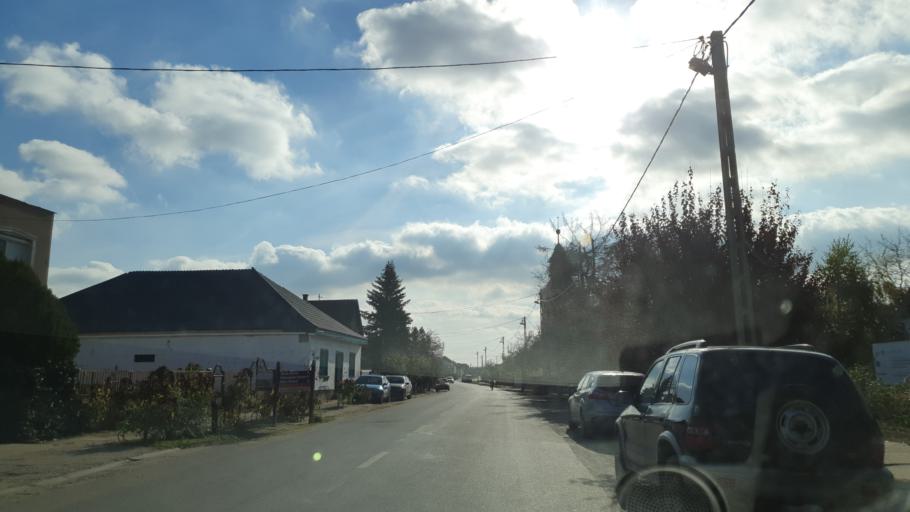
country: HU
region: Szabolcs-Szatmar-Bereg
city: Nyirkarasz
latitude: 48.0985
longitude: 22.0993
